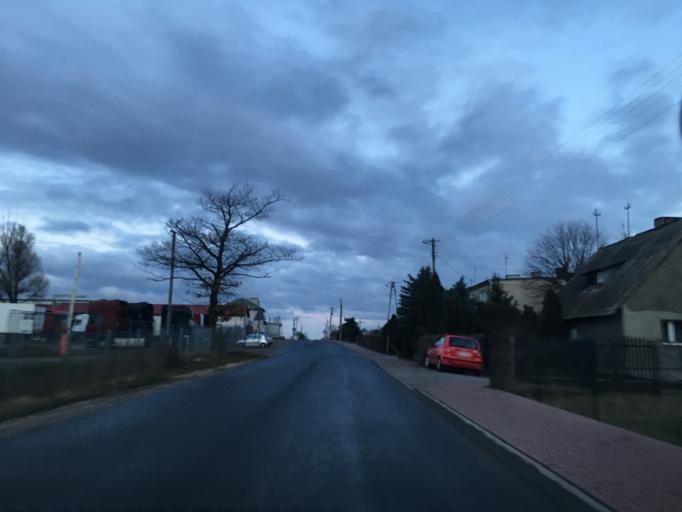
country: PL
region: Masovian Voivodeship
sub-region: Powiat pruszkowski
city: Owczarnia
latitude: 52.0807
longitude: 20.7235
